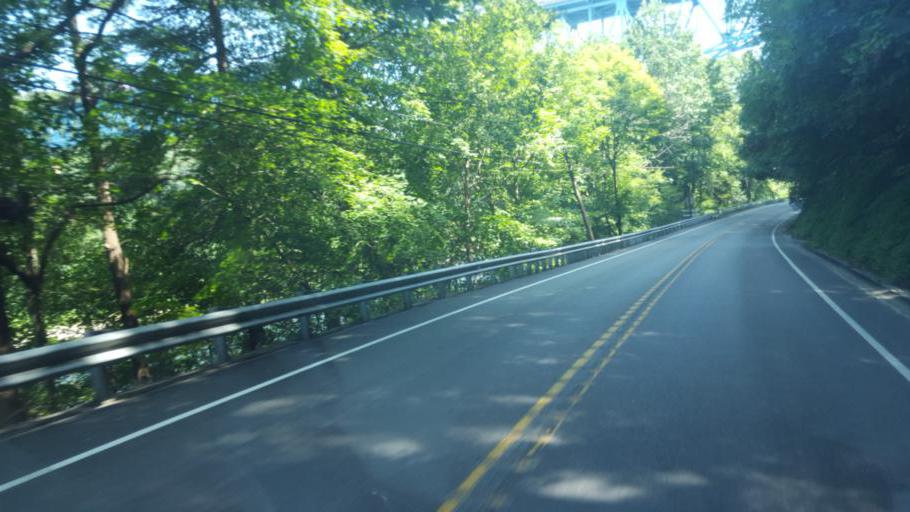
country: US
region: Pennsylvania
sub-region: Clarion County
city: Knox
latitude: 41.1747
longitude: -79.7002
